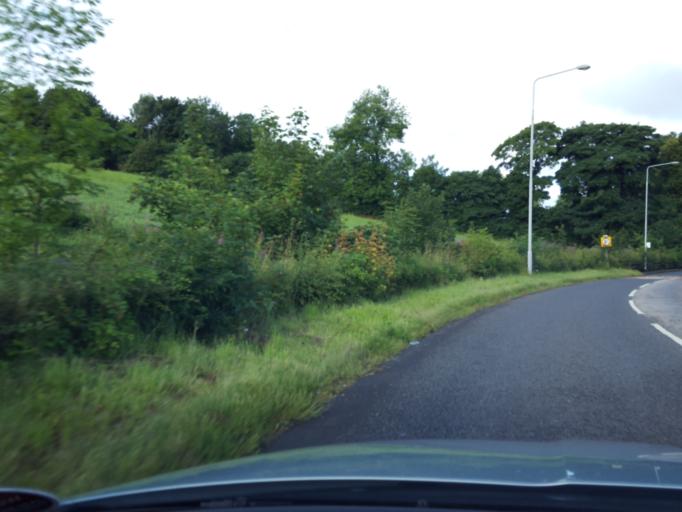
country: GB
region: Scotland
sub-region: West Lothian
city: Linlithgow
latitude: 55.9753
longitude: -3.5825
